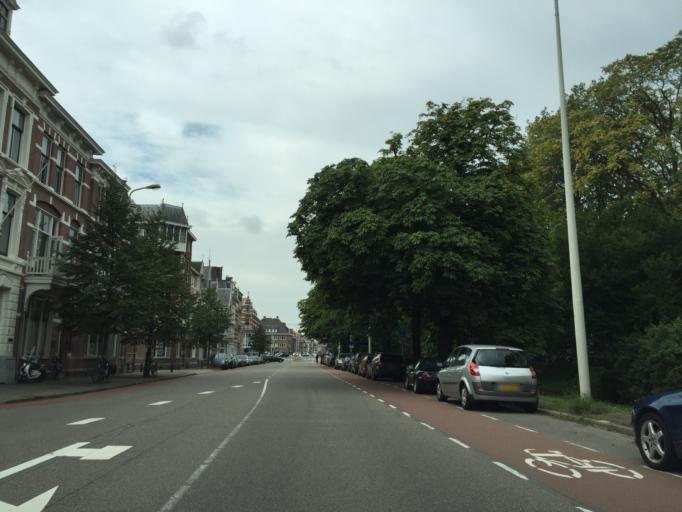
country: NL
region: South Holland
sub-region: Gemeente Den Haag
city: The Hague
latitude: 52.0909
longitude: 4.3152
